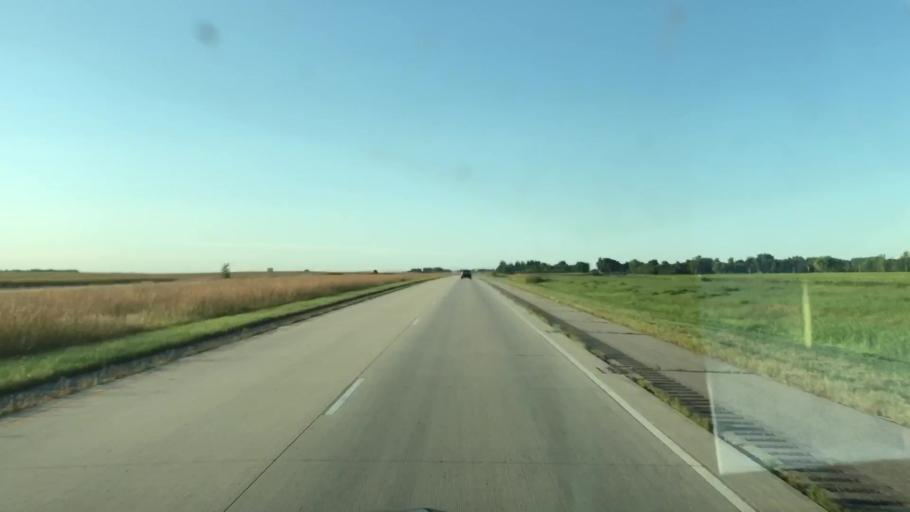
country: US
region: Iowa
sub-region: Osceola County
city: Sibley
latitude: 43.5132
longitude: -95.6835
